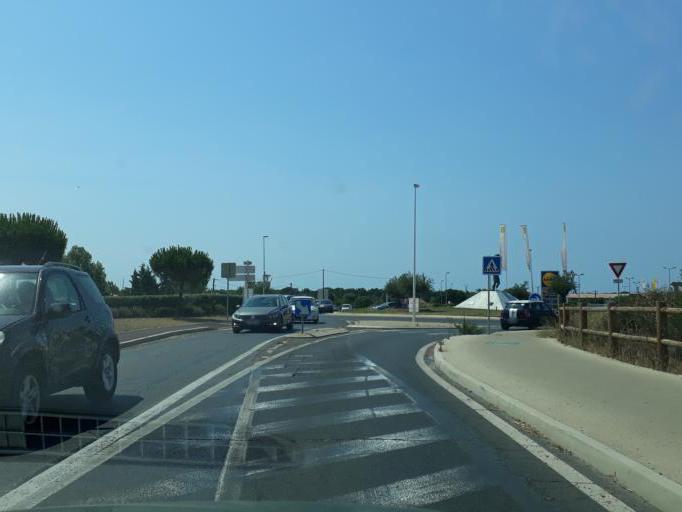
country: FR
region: Languedoc-Roussillon
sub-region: Departement de l'Herault
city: Agde
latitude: 43.2971
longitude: 3.4709
